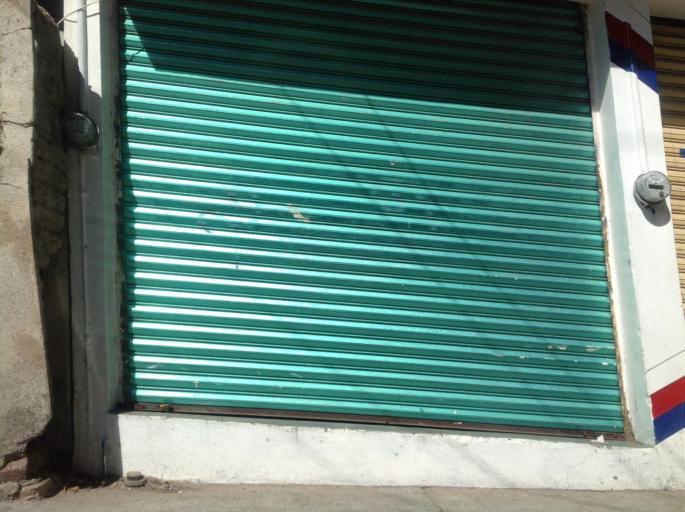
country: MX
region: Oaxaca
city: Ciudad de Huajuapam de Leon
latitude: 17.8106
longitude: -97.7743
